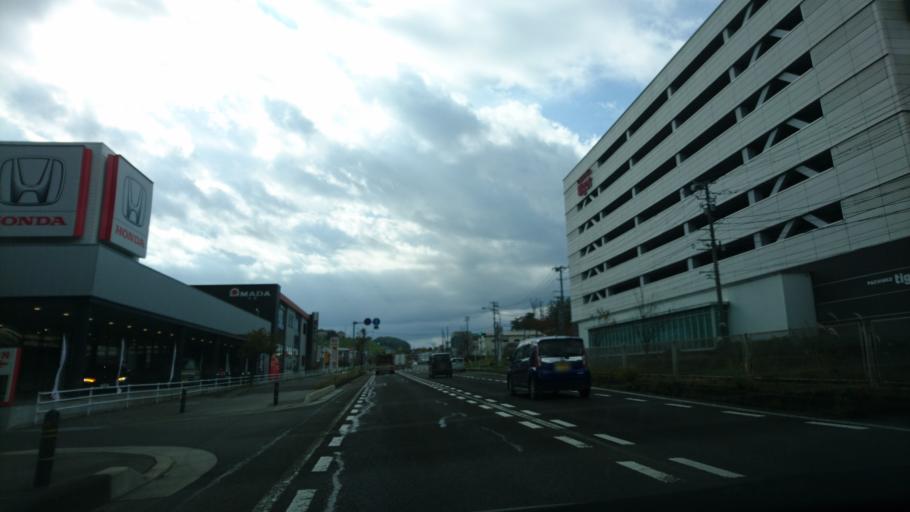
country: JP
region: Miyagi
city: Tomiya
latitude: 38.3714
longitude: 140.8741
